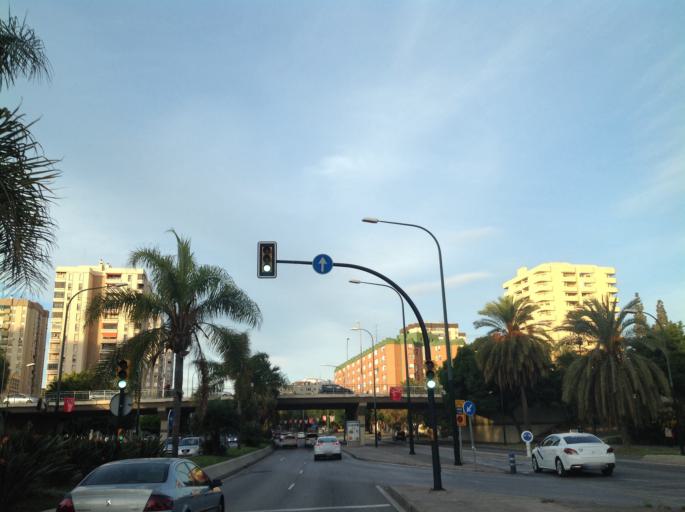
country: ES
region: Andalusia
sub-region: Provincia de Malaga
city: Malaga
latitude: 36.7173
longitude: -4.4357
